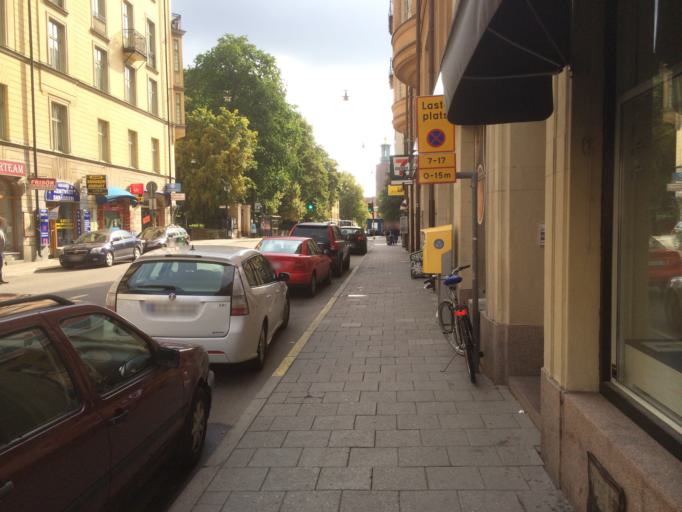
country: SE
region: Stockholm
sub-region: Stockholms Kommun
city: Stockholm
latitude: 59.3286
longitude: 18.0461
